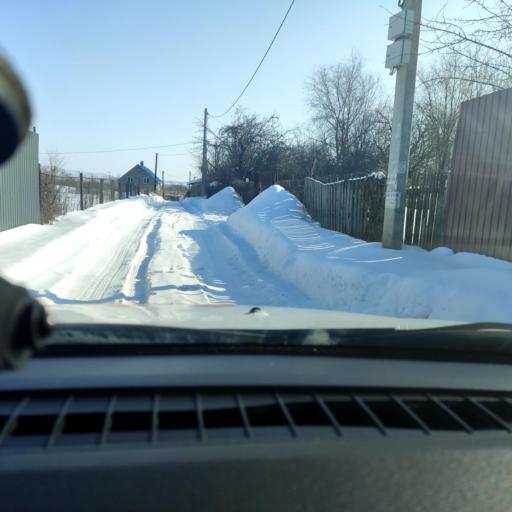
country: RU
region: Samara
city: Samara
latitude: 53.1319
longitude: 50.2568
